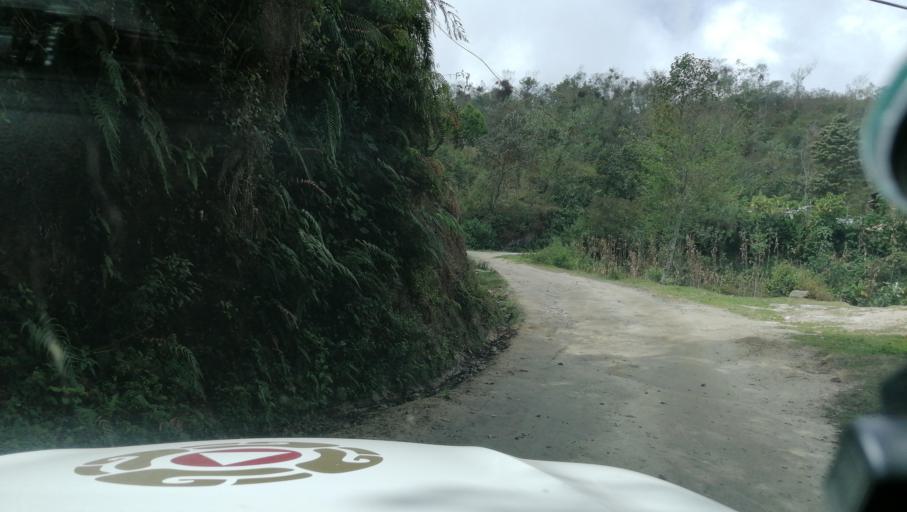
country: MX
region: Chiapas
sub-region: Cacahoatan
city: Benito Juarez
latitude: 15.1987
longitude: -92.2262
